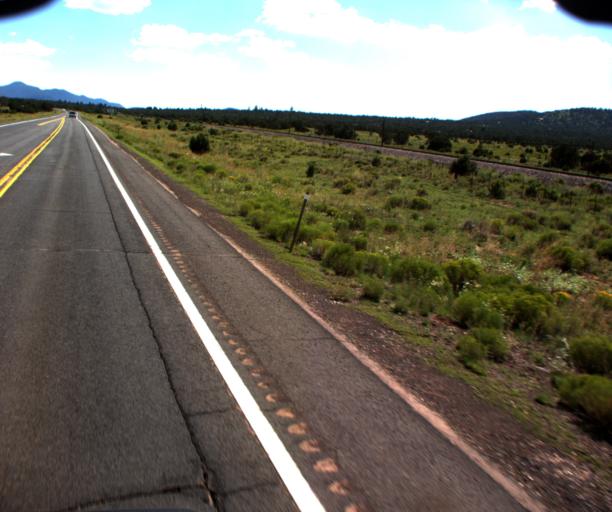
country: US
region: Arizona
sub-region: Coconino County
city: Williams
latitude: 35.3670
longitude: -112.1652
